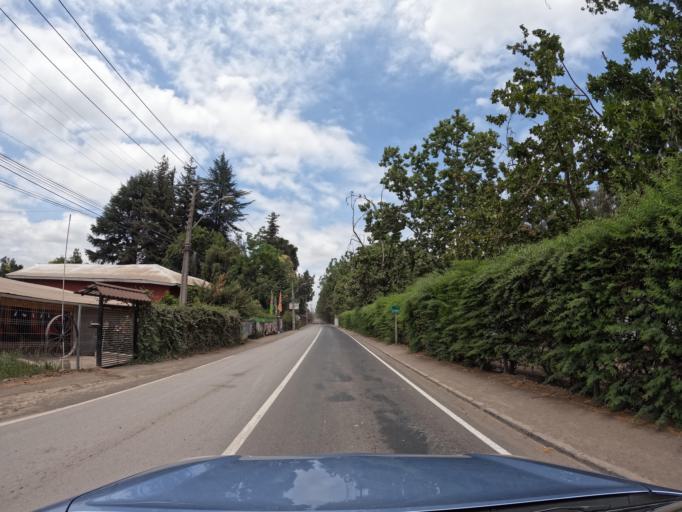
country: CL
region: O'Higgins
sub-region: Provincia de Colchagua
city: Chimbarongo
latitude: -34.7365
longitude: -70.9758
